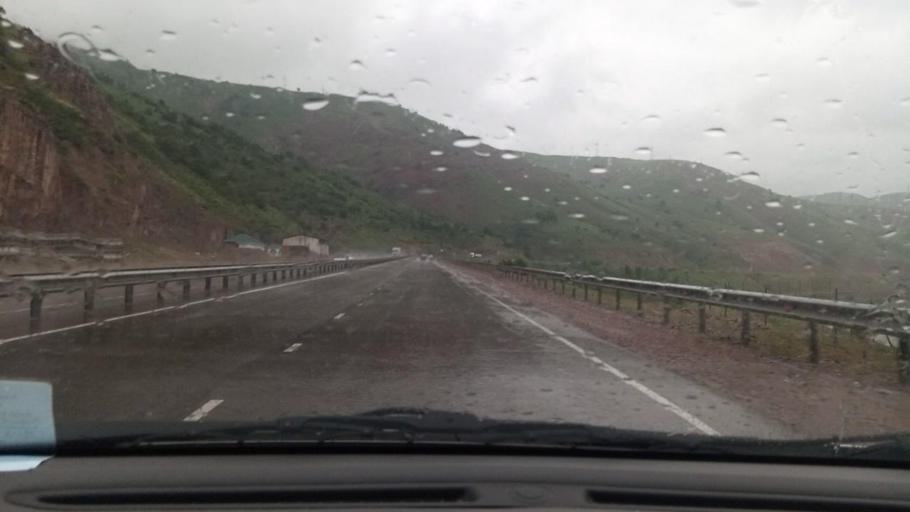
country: UZ
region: Toshkent
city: Angren
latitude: 41.0881
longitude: 70.3220
